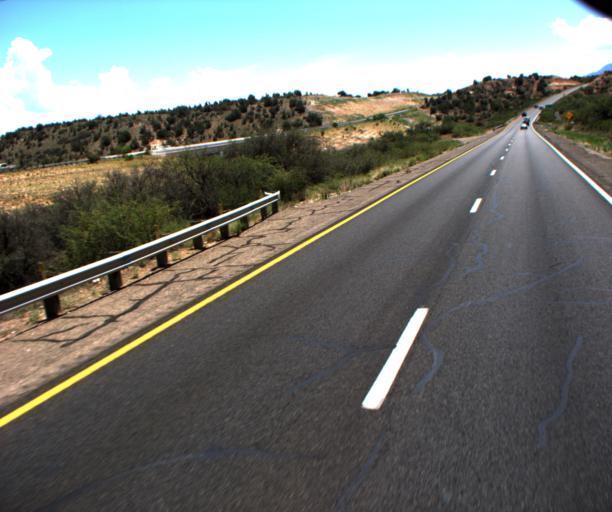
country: US
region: Arizona
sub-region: Yavapai County
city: Verde Village
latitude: 34.6797
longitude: -111.9744
